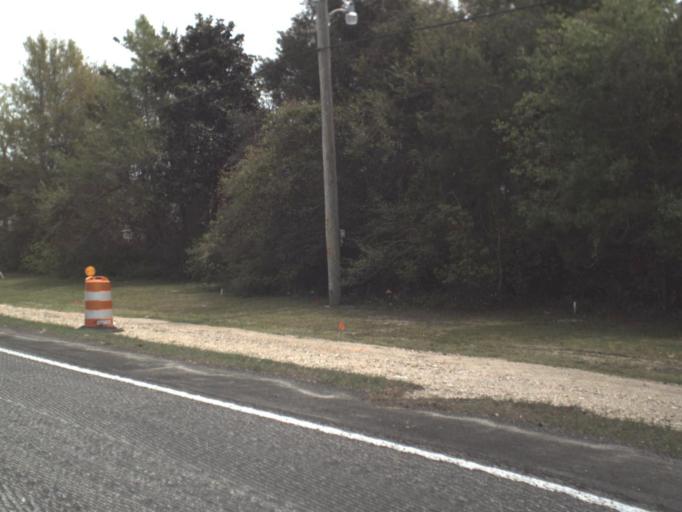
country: US
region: Florida
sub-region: Santa Rosa County
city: Navarre
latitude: 30.4096
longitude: -86.8021
